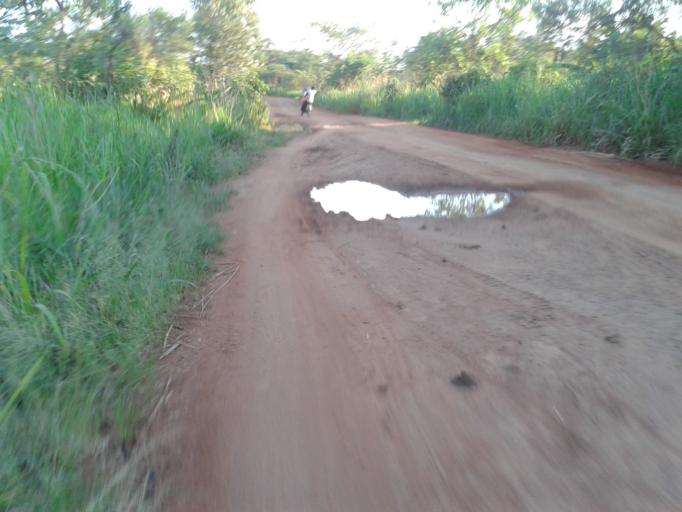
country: UG
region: Northern Region
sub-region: Gulu District
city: Gulu
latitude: 2.7829
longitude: 32.3683
